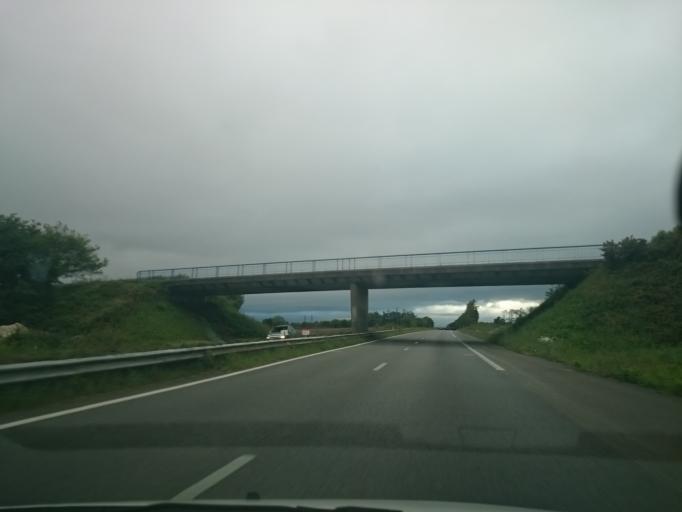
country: FR
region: Brittany
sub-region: Departement du Finistere
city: Melgven
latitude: 47.9019
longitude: -3.8407
